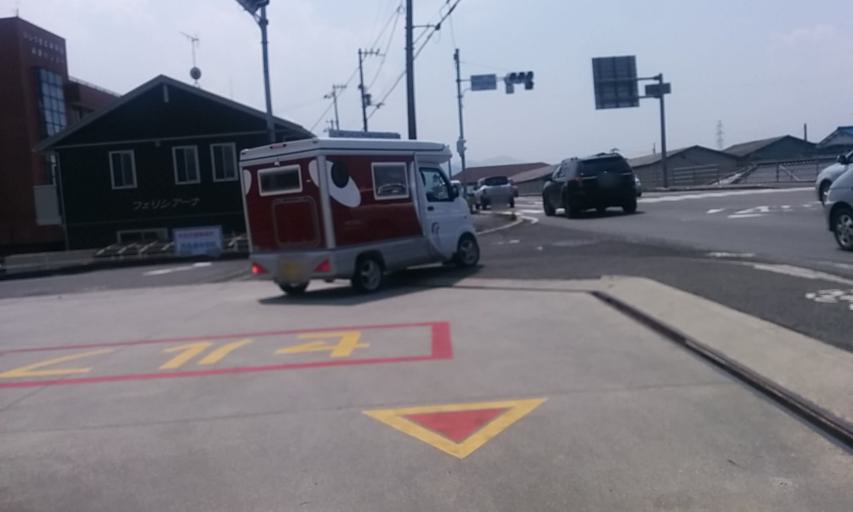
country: JP
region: Ehime
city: Saijo
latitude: 33.9061
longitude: 133.1867
